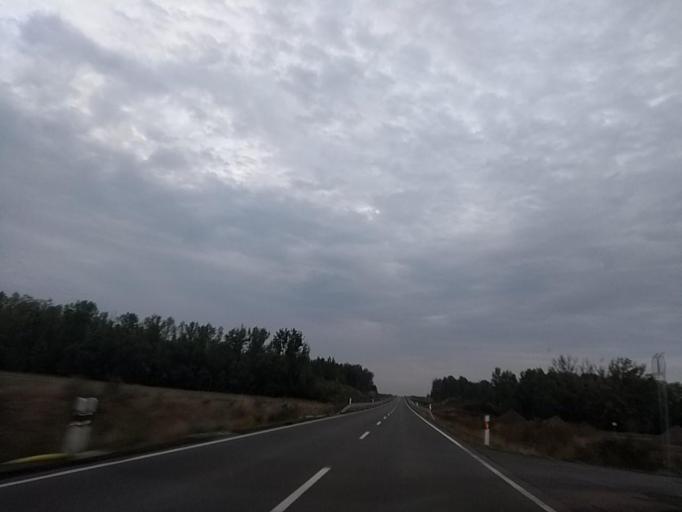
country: DE
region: Saxony-Anhalt
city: Muschwitz
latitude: 51.1731
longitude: 12.1228
